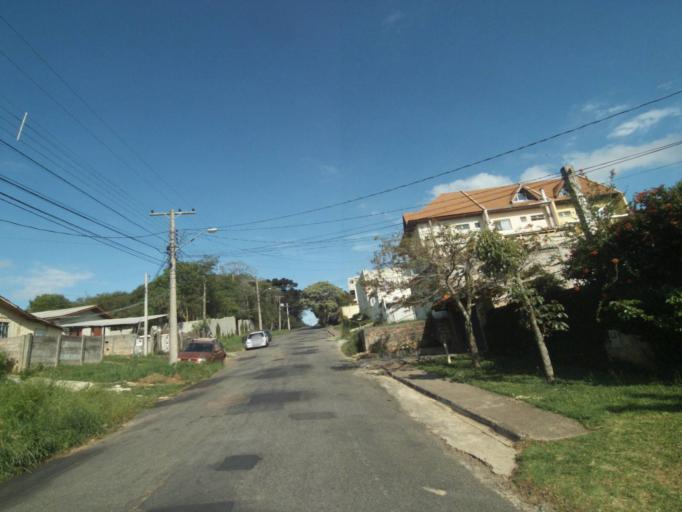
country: BR
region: Parana
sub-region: Curitiba
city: Curitiba
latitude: -25.3978
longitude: -49.2997
